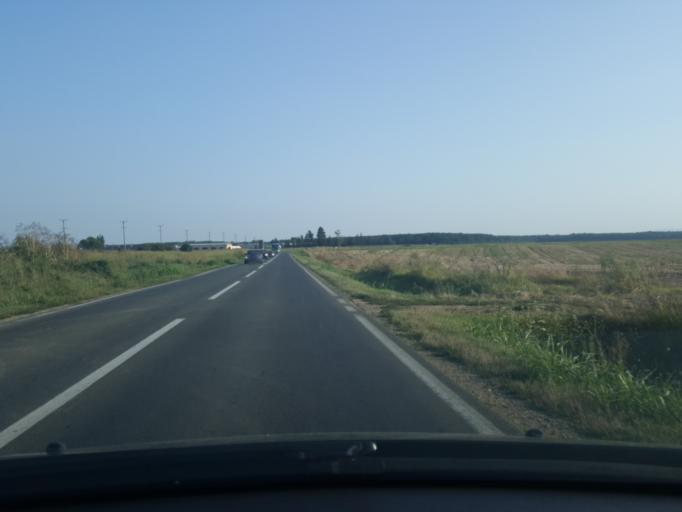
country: RS
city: Hrtkovci
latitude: 44.8543
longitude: 19.7710
